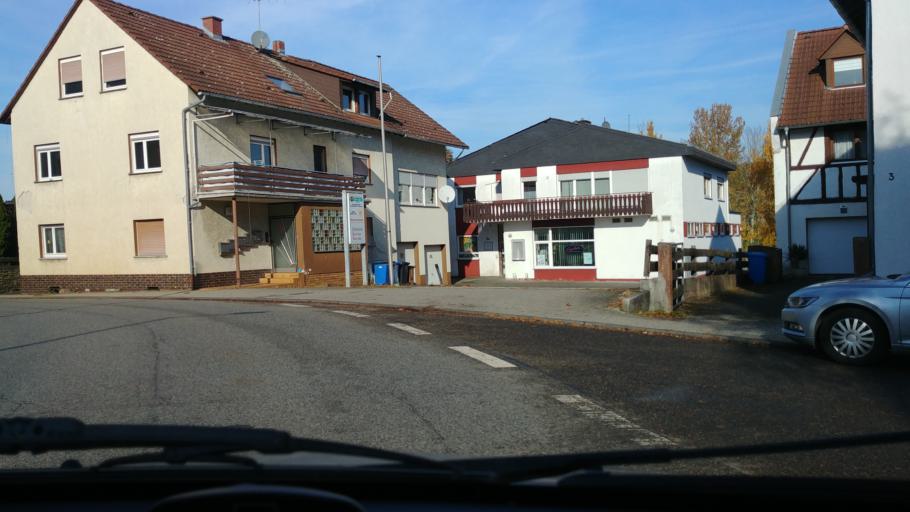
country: DE
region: Hesse
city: Burg Hohenstein
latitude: 50.1937
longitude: 8.1002
